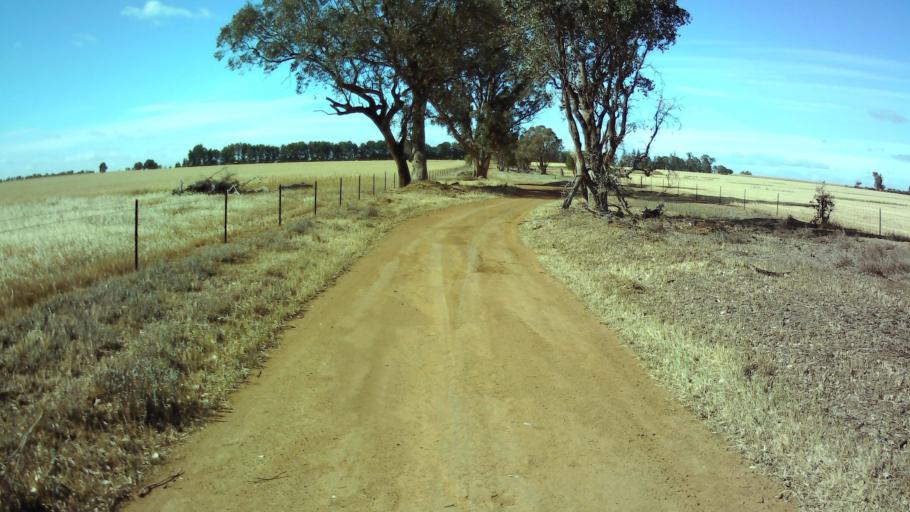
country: AU
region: New South Wales
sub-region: Weddin
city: Grenfell
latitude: -34.0556
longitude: 148.2681
